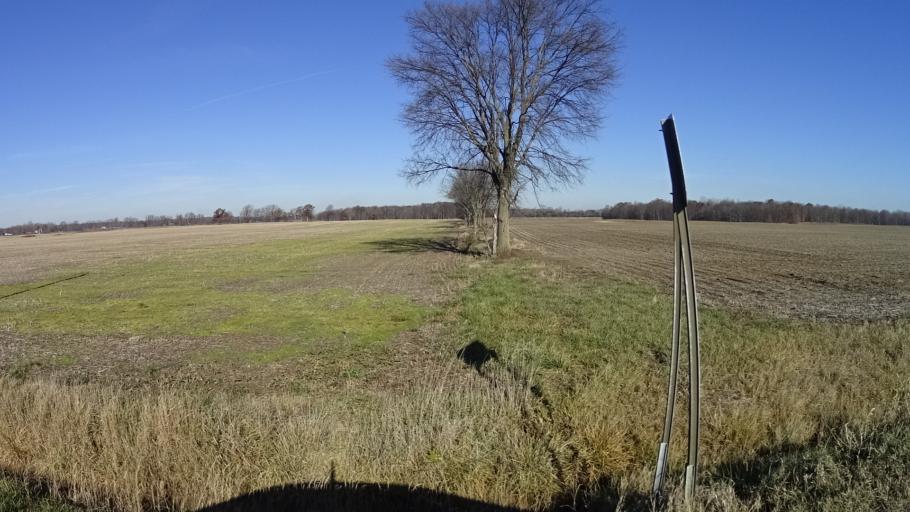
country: US
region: Ohio
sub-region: Huron County
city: New London
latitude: 41.1028
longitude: -82.3377
